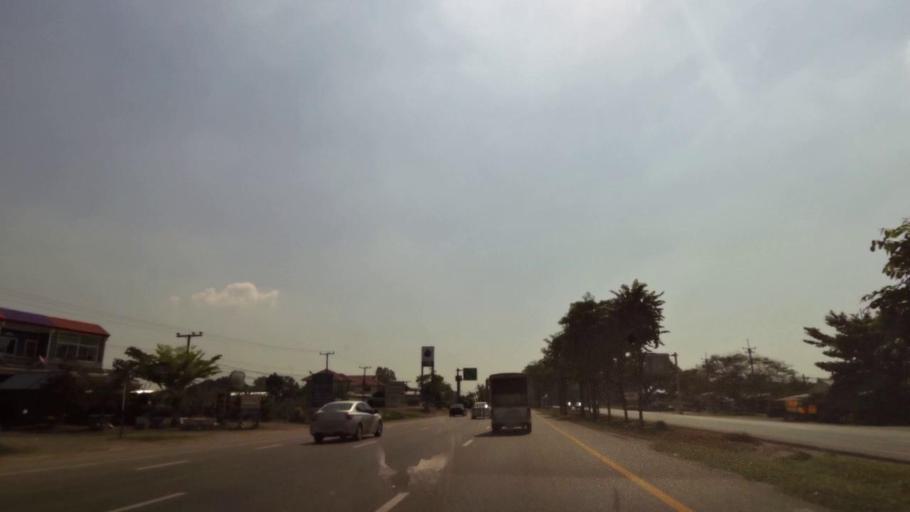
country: TH
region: Phichit
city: Bueng Na Rang
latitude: 16.1202
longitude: 100.1257
